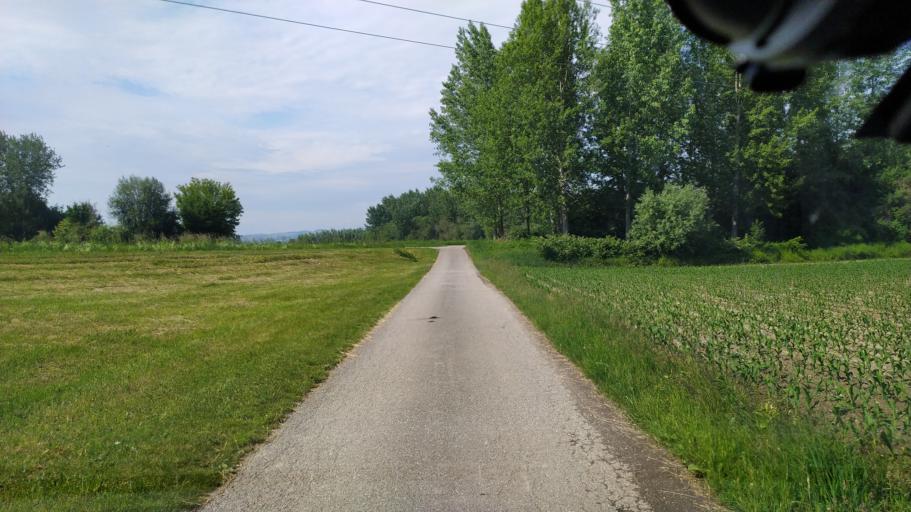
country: AT
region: Lower Austria
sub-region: Politischer Bezirk Amstetten
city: Strengberg
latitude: 48.1749
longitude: 14.6934
